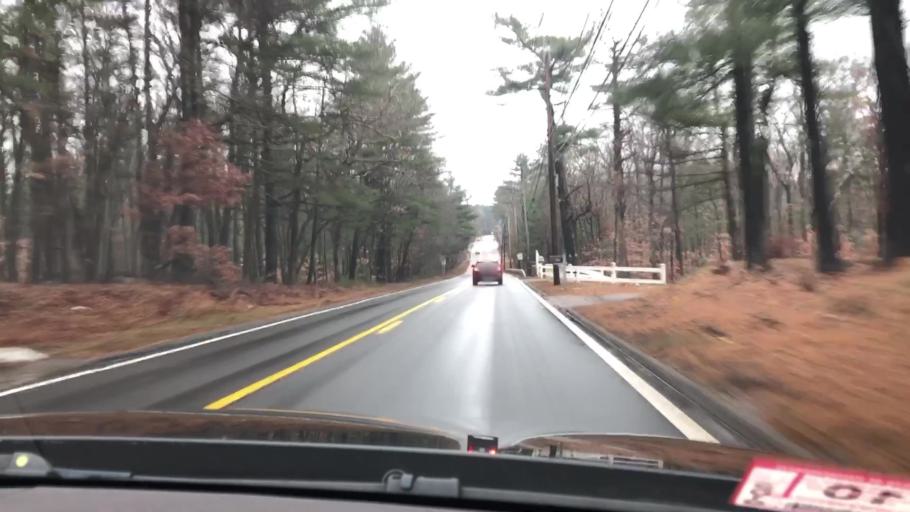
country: US
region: Massachusetts
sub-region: Norfolk County
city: Norfolk
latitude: 42.1083
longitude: -71.2857
